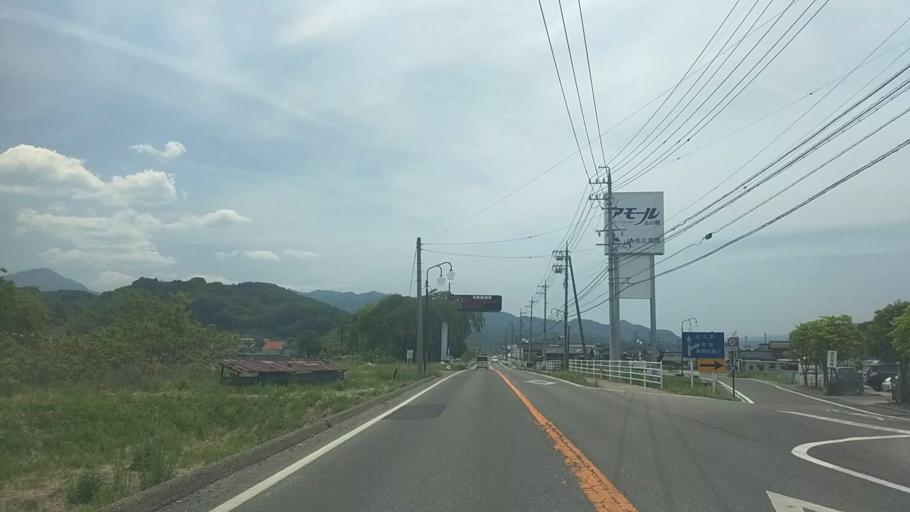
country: JP
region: Nagano
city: Saku
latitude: 36.1715
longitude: 138.4857
